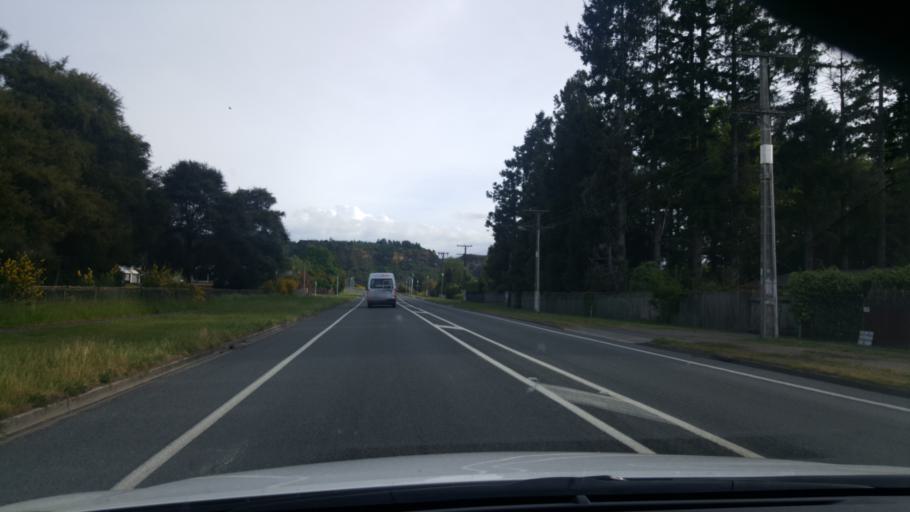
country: NZ
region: Waikato
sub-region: Taupo District
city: Taupo
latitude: -38.7931
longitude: 176.0758
